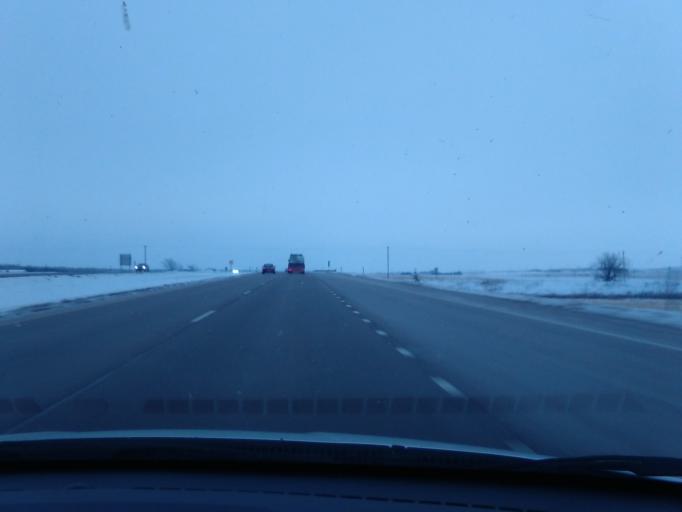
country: US
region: Nebraska
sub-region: Lincoln County
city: Sutherland
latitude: 41.1114
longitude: -101.3518
